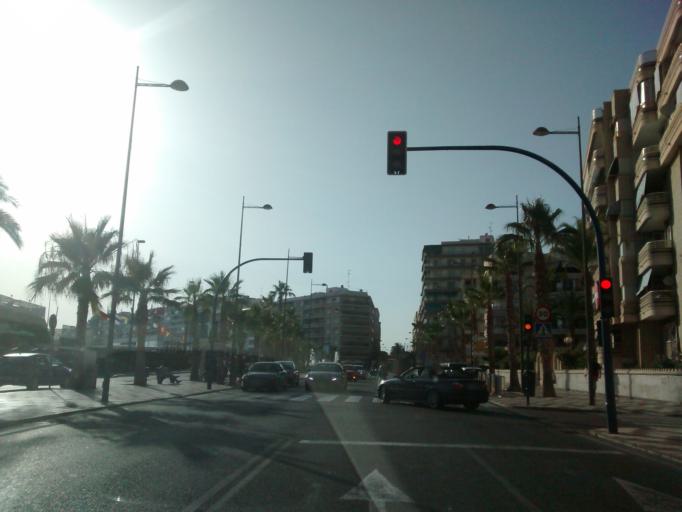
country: ES
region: Valencia
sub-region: Provincia de Alicante
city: Santa Pola
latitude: 38.1911
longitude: -0.5587
